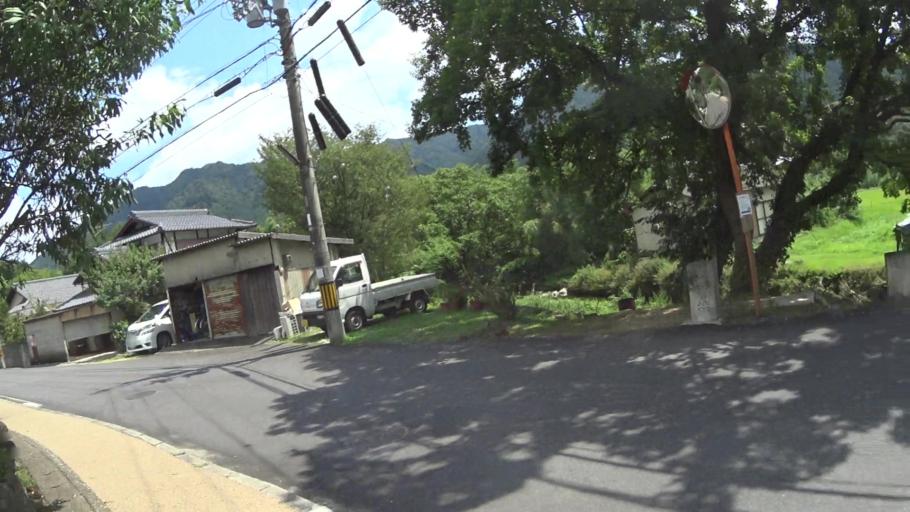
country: JP
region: Shiga Prefecture
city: Kitahama
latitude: 35.1187
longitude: 135.8263
